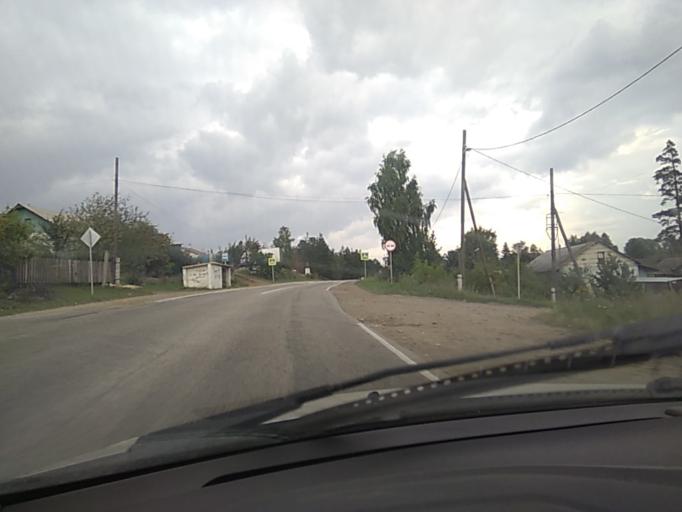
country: RU
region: Chelyabinsk
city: Kyshtym
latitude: 55.7214
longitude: 60.5113
